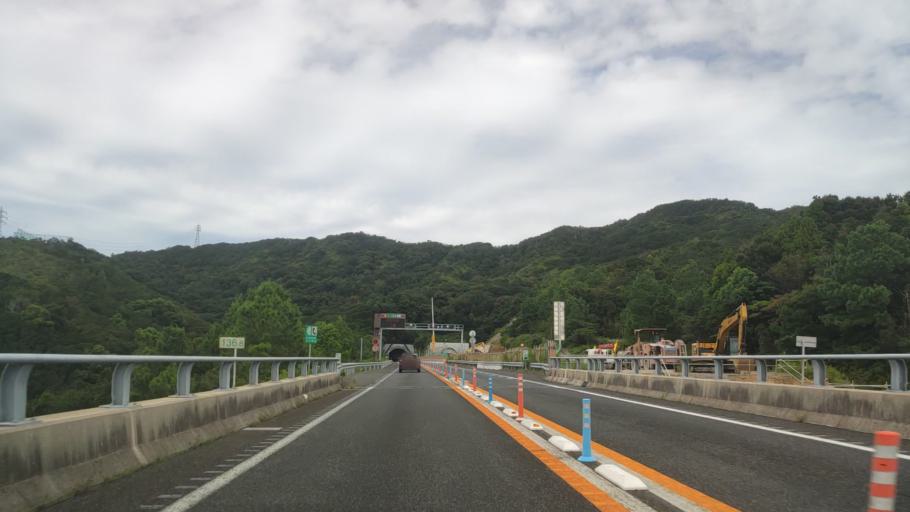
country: JP
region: Wakayama
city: Gobo
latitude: 33.8463
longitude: 135.2179
